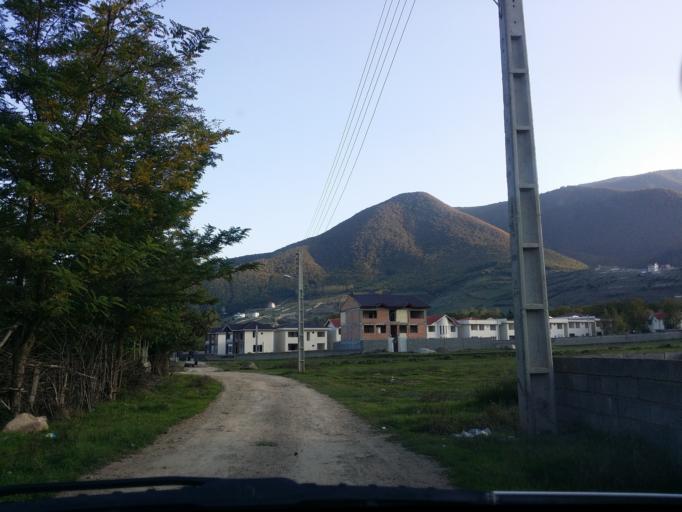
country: IR
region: Mazandaran
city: `Abbasabad
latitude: 36.5130
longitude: 51.1821
